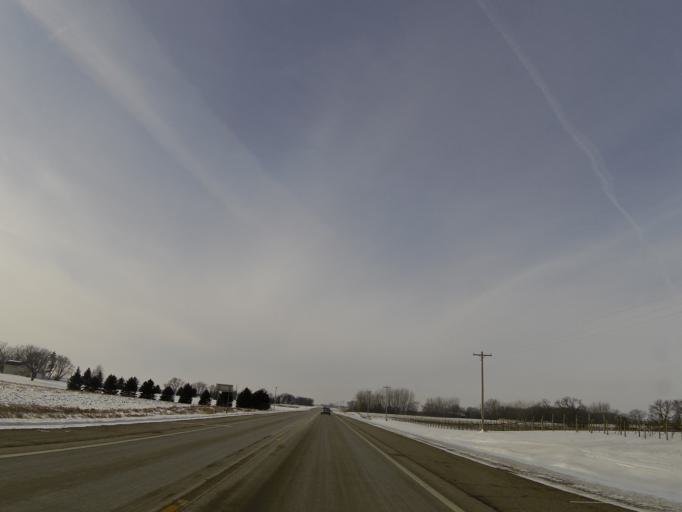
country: US
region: Minnesota
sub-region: McLeod County
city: Hutchinson
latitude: 44.8926
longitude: -94.2944
